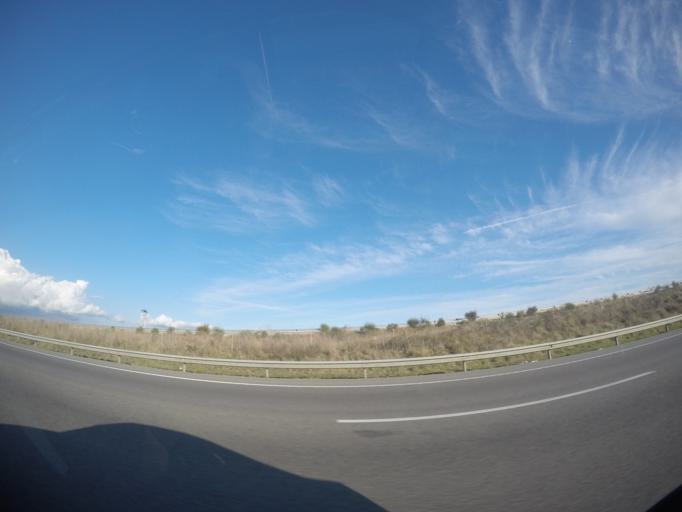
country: ES
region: Catalonia
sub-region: Provincia de Barcelona
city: Vilafranca del Penedes
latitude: 41.3360
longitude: 1.7153
